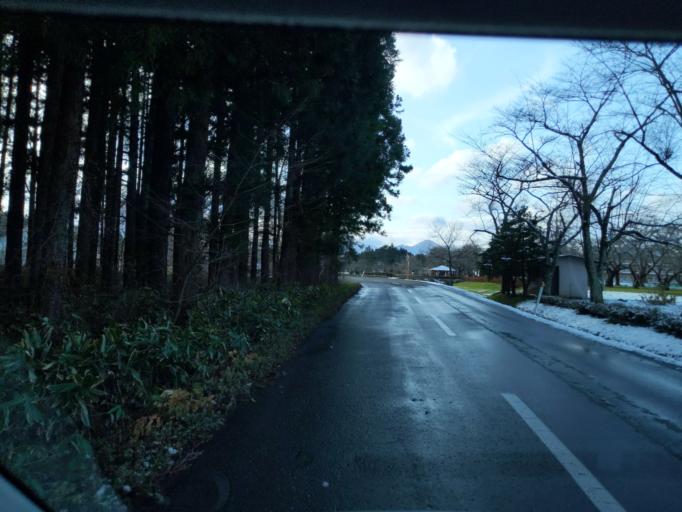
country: JP
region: Iwate
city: Kitakami
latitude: 39.2356
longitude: 141.0477
